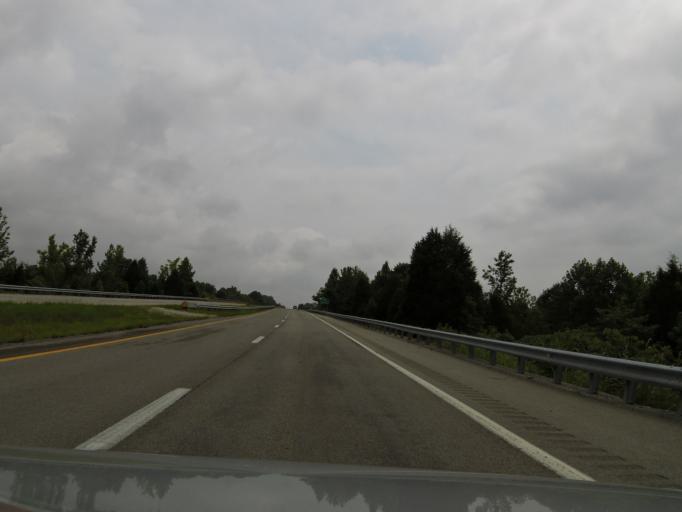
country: US
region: Kentucky
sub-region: Muhlenberg County
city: Central City
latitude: 37.3215
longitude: -86.9950
